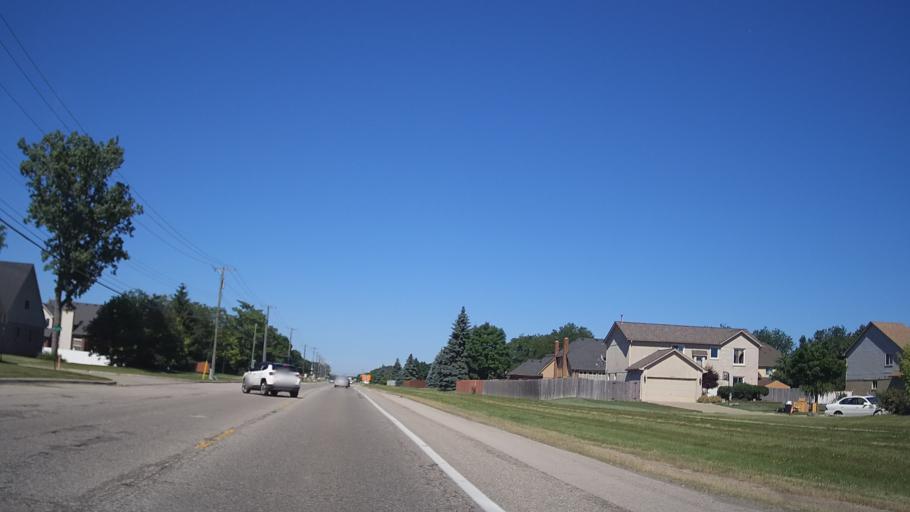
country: US
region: Michigan
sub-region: Macomb County
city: Sterling Heights
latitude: 42.5938
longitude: -83.0629
